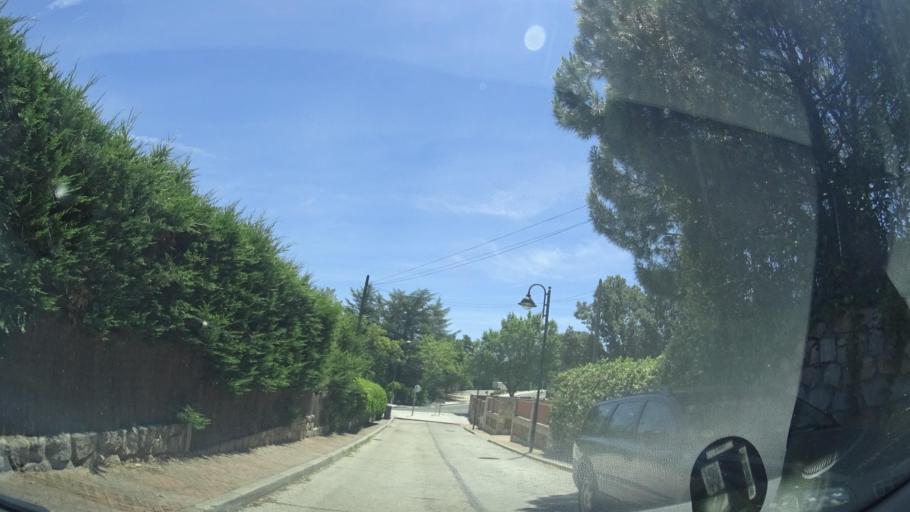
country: ES
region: Madrid
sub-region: Provincia de Madrid
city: Galapagar
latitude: 40.5944
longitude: -3.9878
